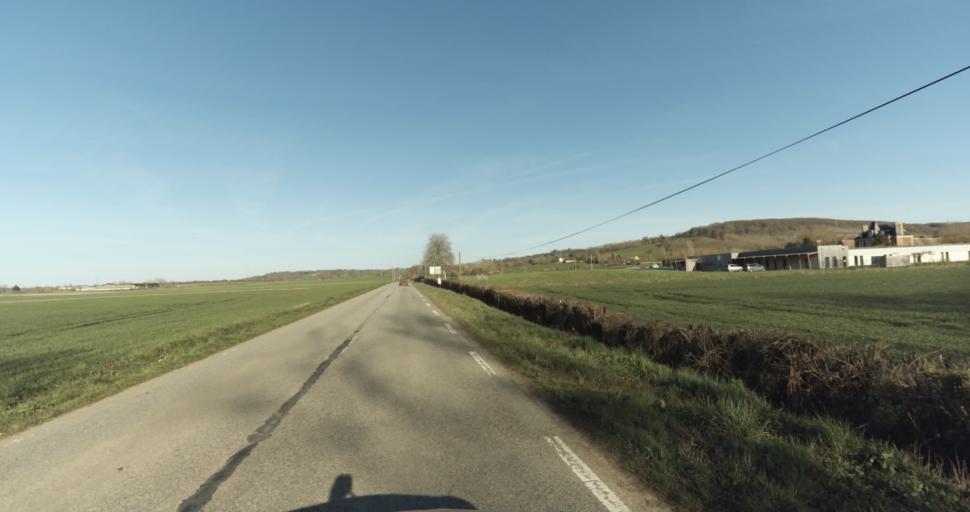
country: FR
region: Lower Normandy
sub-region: Departement du Calvados
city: Saint-Pierre-sur-Dives
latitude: 49.0167
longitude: 0.0196
